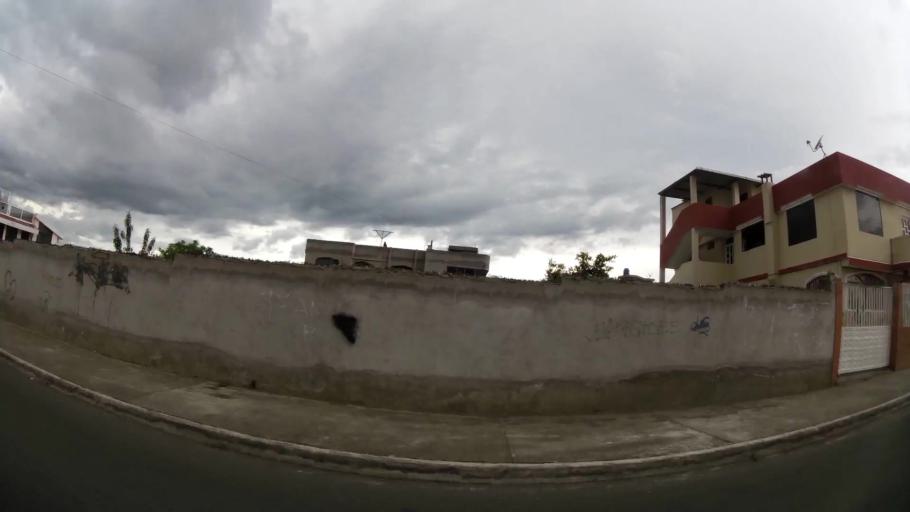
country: EC
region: Tungurahua
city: Ambato
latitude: -1.2682
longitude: -78.6202
